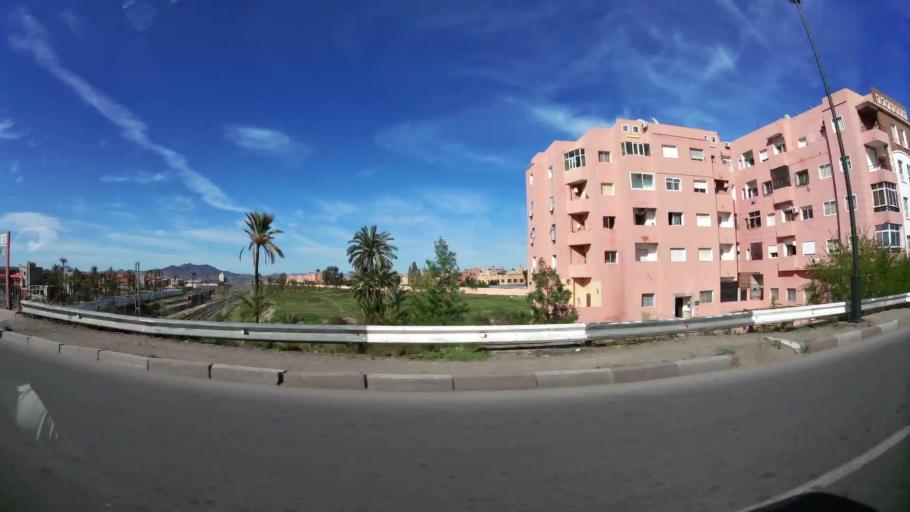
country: MA
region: Marrakech-Tensift-Al Haouz
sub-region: Marrakech
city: Marrakesh
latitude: 31.6656
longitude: -8.0338
